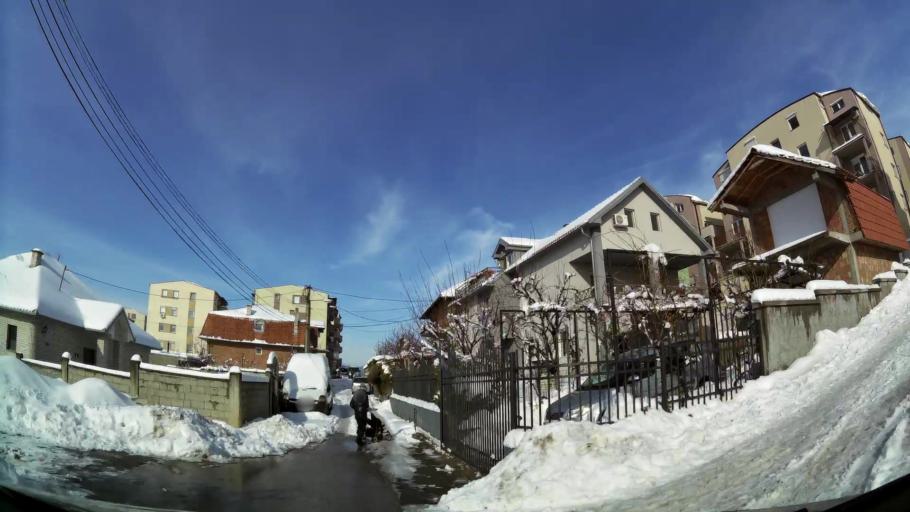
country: RS
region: Central Serbia
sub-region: Belgrade
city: Palilula
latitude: 44.8025
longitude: 20.5293
